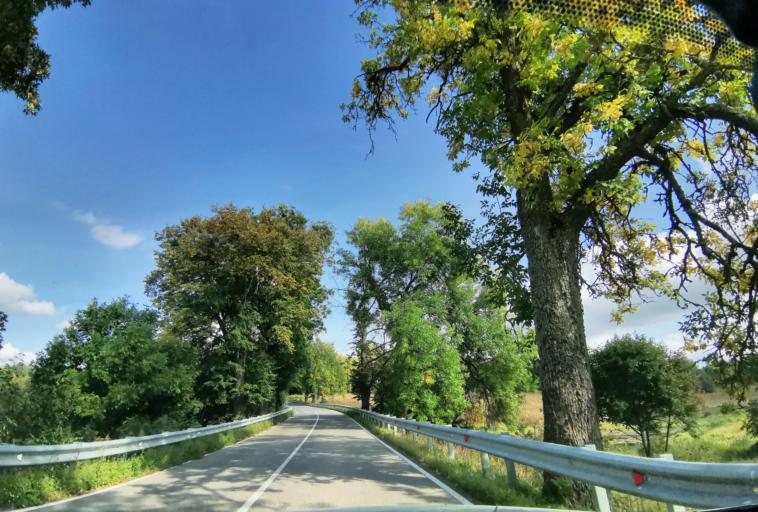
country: PL
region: Warmian-Masurian Voivodeship
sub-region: Powiat goldapski
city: Goldap
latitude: 54.4583
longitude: 22.3778
